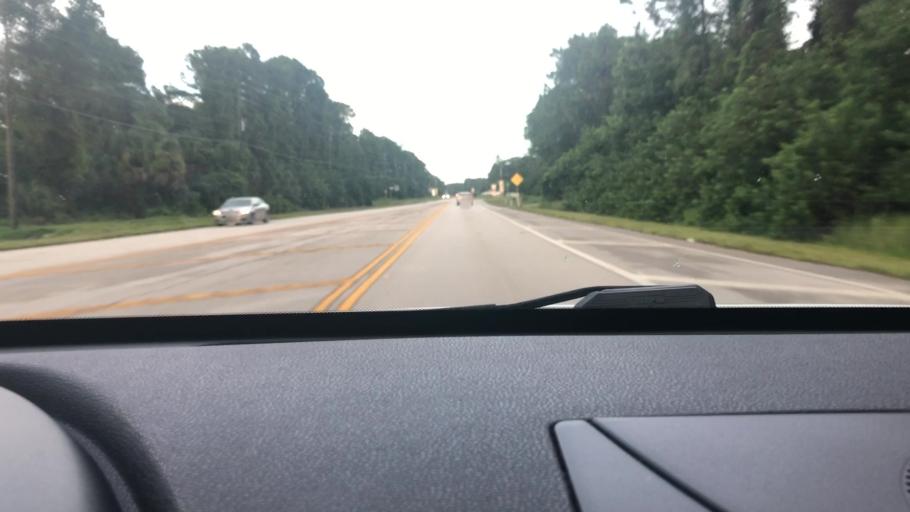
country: US
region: Florida
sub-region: Sarasota County
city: North Port
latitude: 27.0684
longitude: -82.1521
